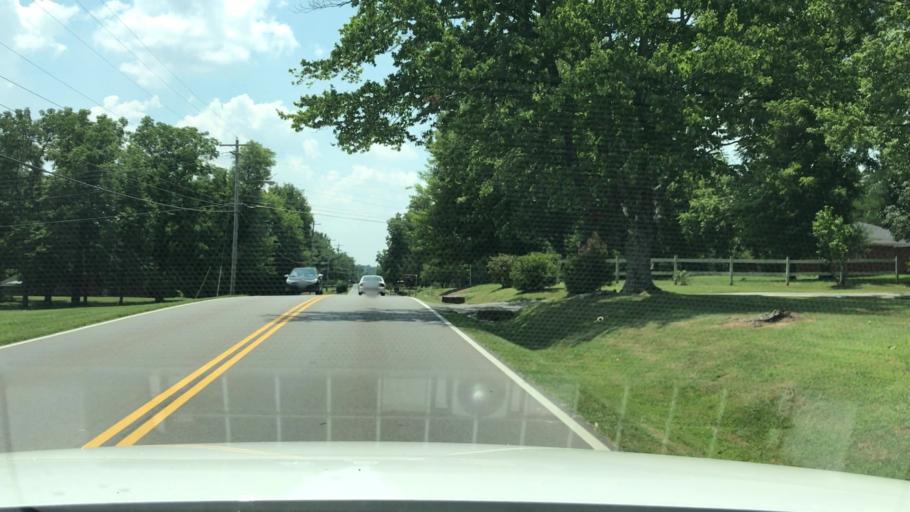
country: US
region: Tennessee
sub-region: Sumner County
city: Gallatin
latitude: 36.3760
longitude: -86.4680
